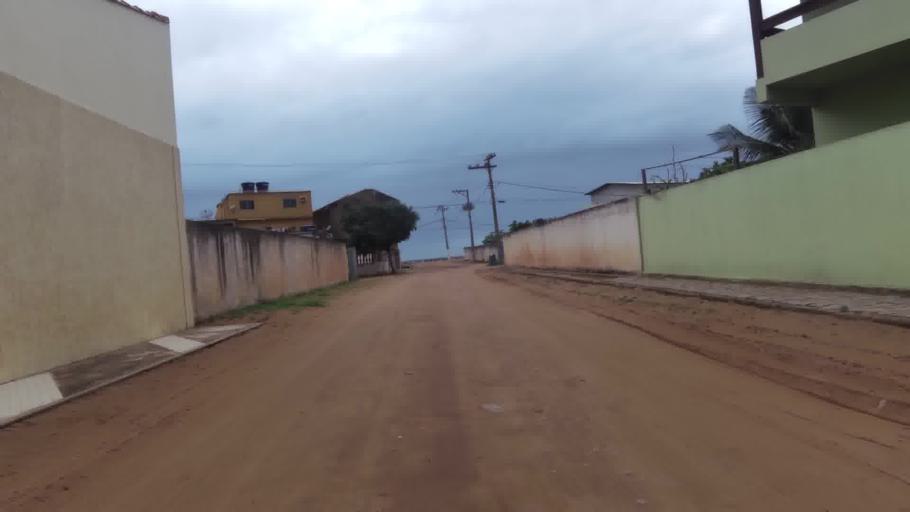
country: BR
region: Espirito Santo
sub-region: Marataizes
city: Marataizes
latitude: -21.0515
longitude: -40.8325
